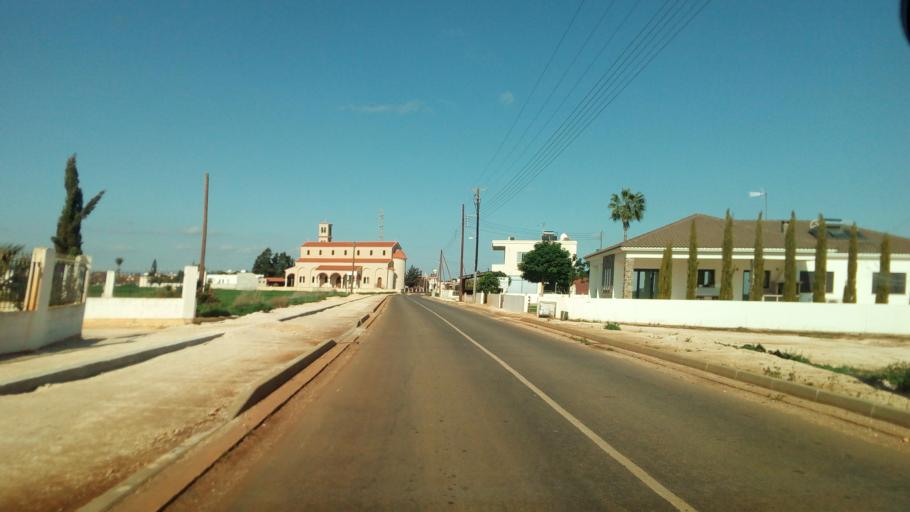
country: CY
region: Ammochostos
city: Avgorou
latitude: 35.0231
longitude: 33.8406
